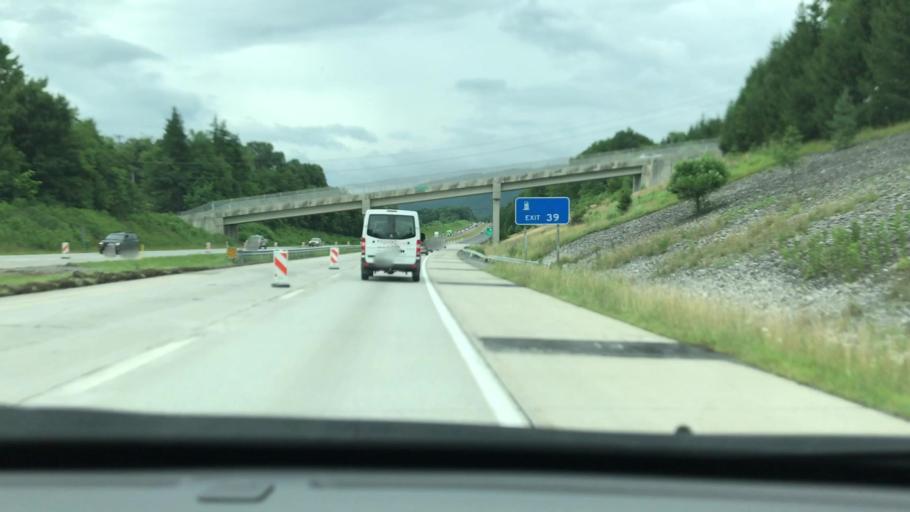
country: US
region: Pennsylvania
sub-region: Blair County
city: Greenwood
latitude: 40.5381
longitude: -78.3475
